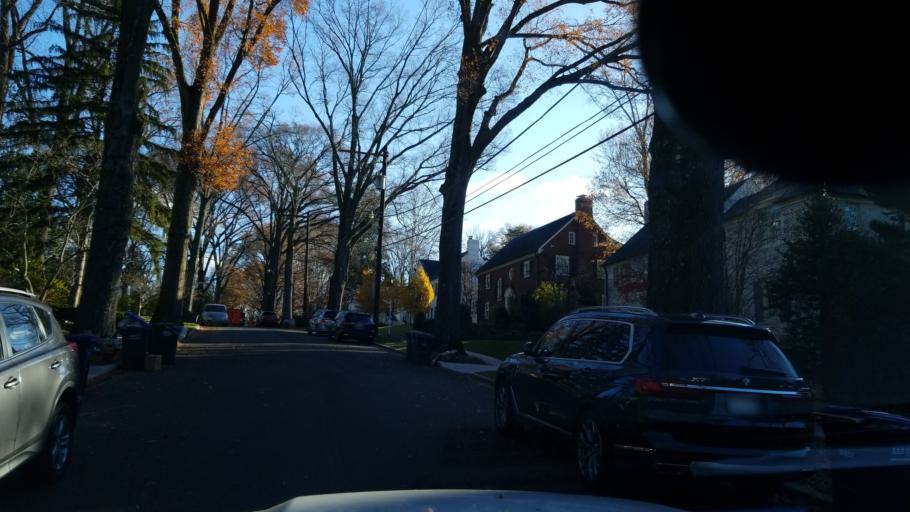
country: US
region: Maryland
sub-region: Montgomery County
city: Brookmont
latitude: 38.9323
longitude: -77.1021
